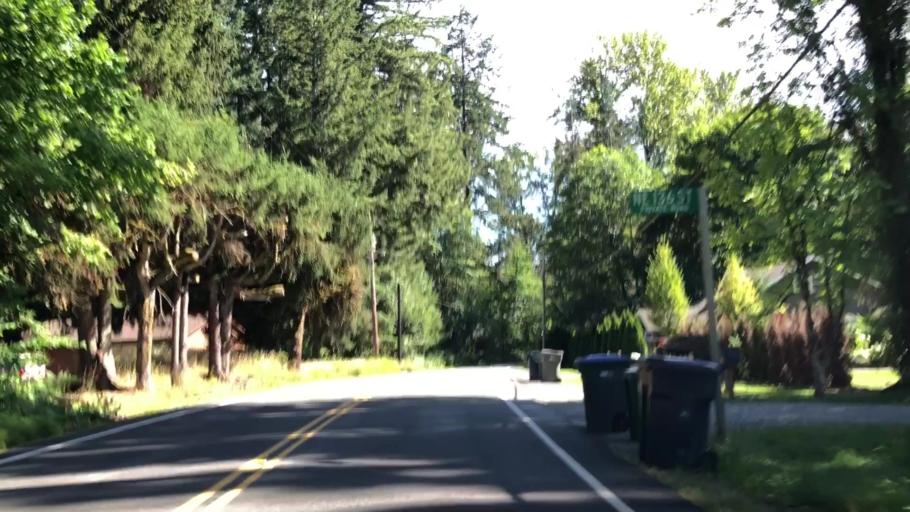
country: US
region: Washington
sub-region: King County
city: Cottage Lake
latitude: 47.7216
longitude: -122.0781
